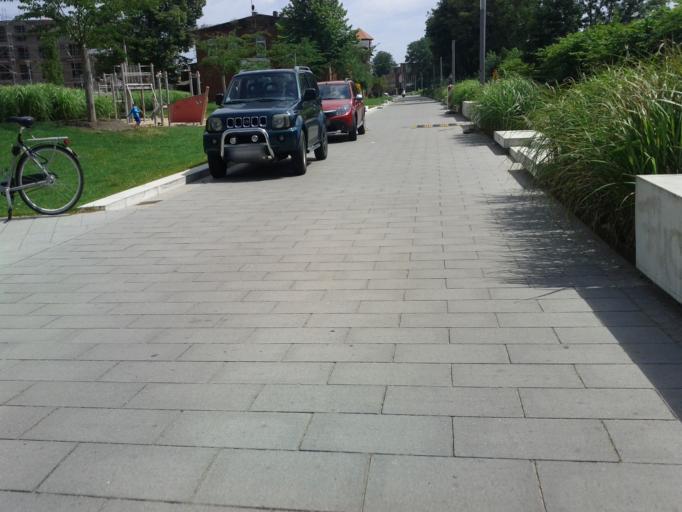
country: DE
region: Lower Saxony
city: Oldenburg
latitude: 53.1406
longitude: 8.2277
